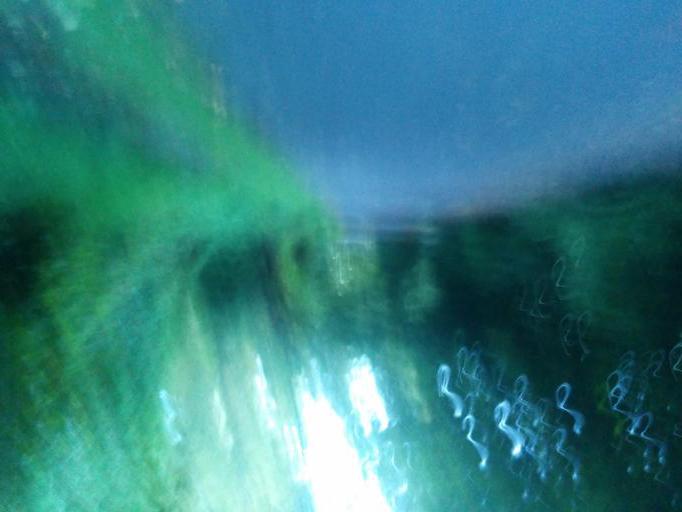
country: US
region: Washington
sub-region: King County
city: Lake Forest Park
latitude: 47.7273
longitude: -122.2814
